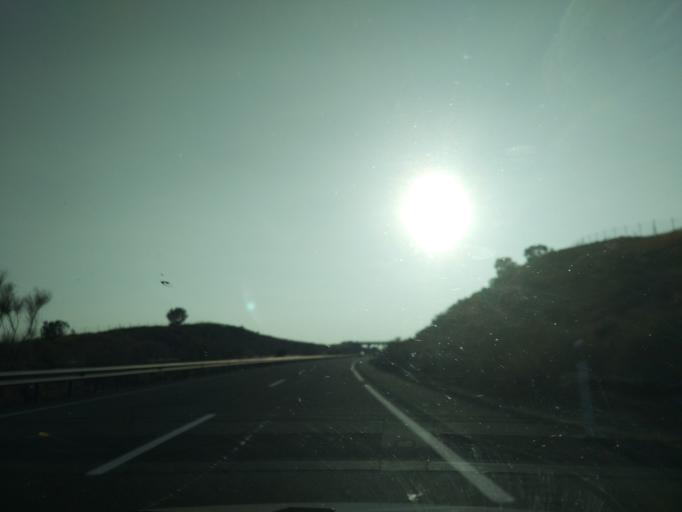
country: ES
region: Castille and Leon
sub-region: Provincia de Segovia
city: Villacastin
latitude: 40.7516
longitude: -4.4594
